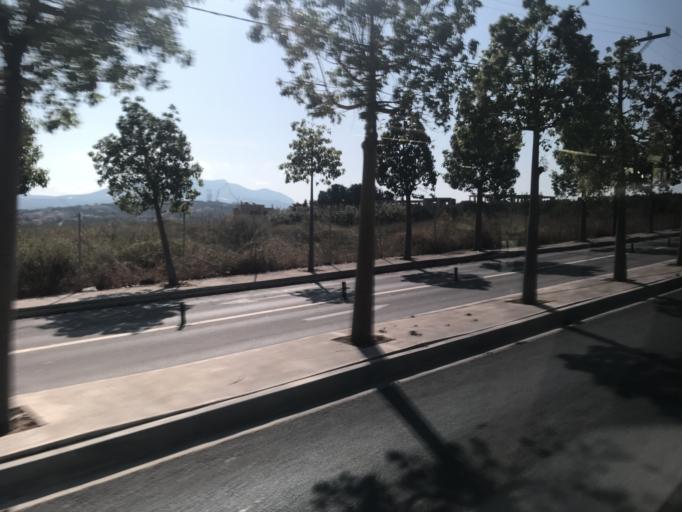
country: GR
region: Crete
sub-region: Nomos Irakleiou
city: Gazi
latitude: 35.3034
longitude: 25.0847
